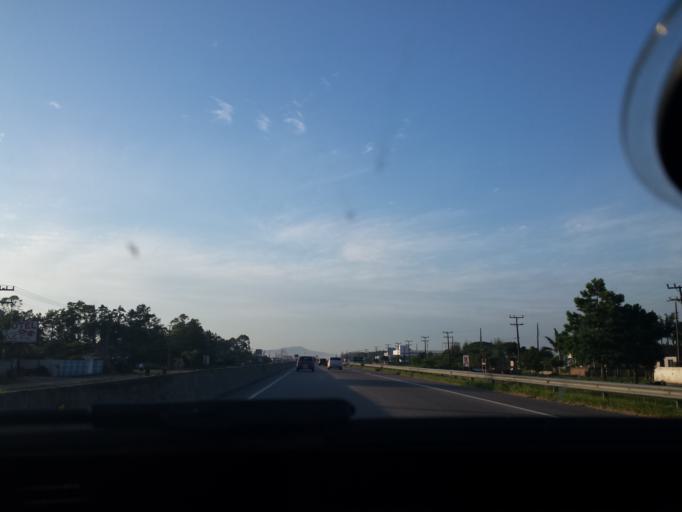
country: BR
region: Santa Catarina
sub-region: Imbituba
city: Imbituba
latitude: -28.1358
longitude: -48.6922
